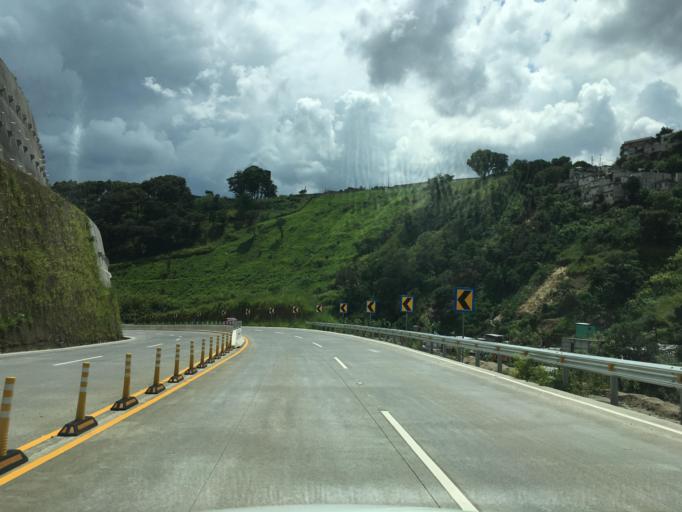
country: GT
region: Guatemala
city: Santa Catarina Pinula
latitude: 14.5551
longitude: -90.5329
